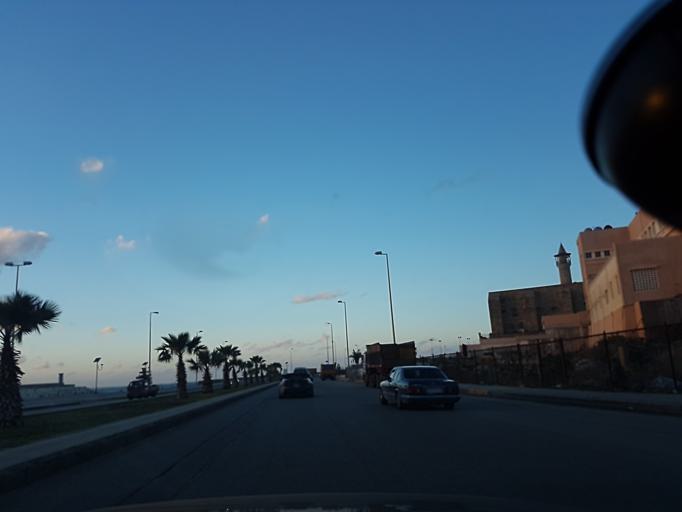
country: LB
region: Liban-Sud
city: Sidon
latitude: 33.5606
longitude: 35.3681
